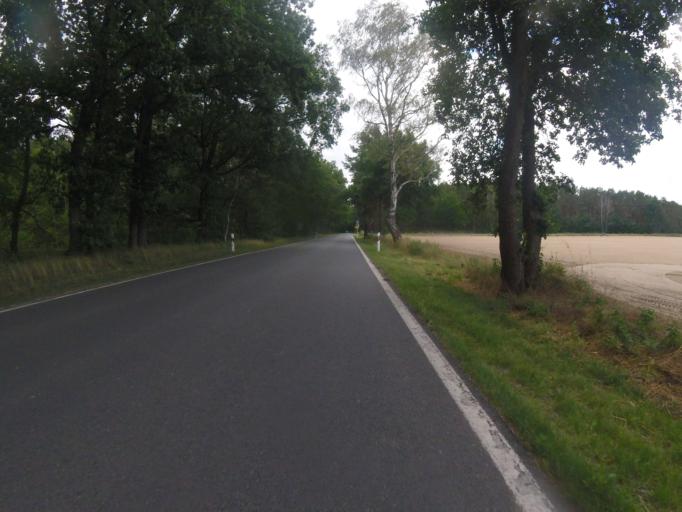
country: DE
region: Brandenburg
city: Bestensee
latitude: 52.2647
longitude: 13.7337
